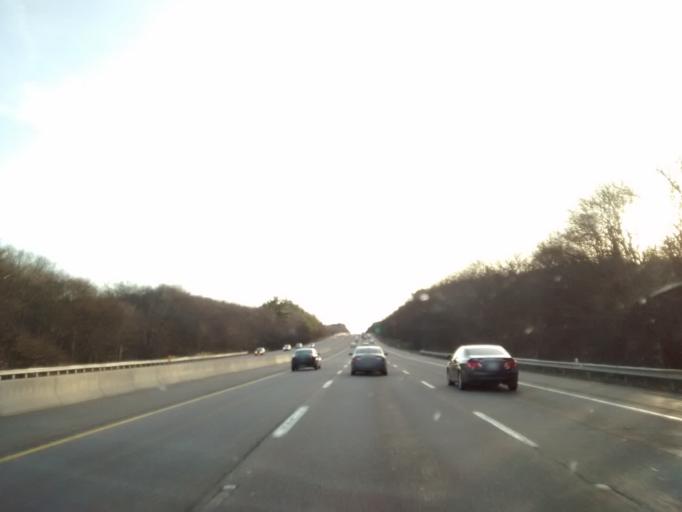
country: US
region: Massachusetts
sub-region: Worcester County
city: Cordaville
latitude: 42.2777
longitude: -71.5269
